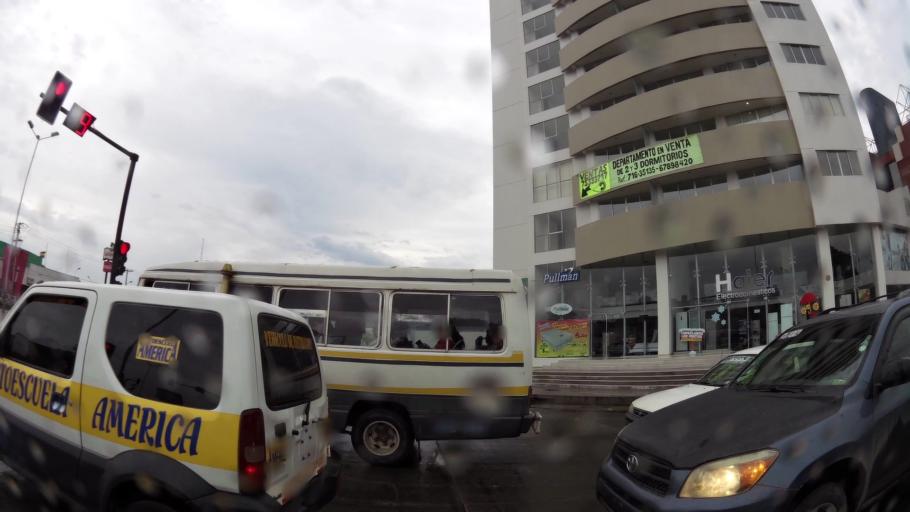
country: BO
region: Santa Cruz
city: Santa Cruz de la Sierra
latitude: -17.7744
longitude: -63.1663
